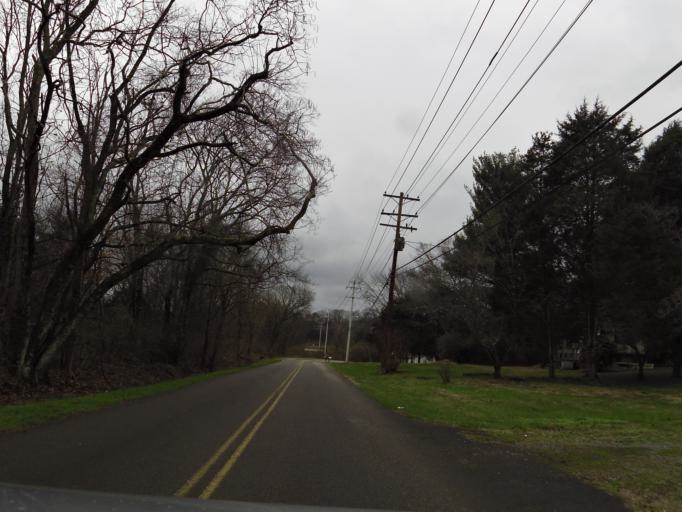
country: US
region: Tennessee
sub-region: Knox County
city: Knoxville
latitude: 35.9888
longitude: -84.0417
